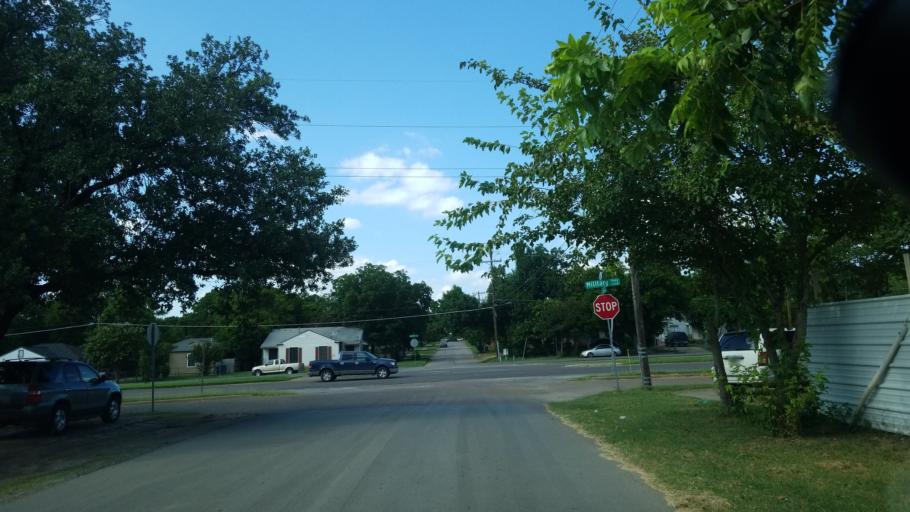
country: US
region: Texas
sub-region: Dallas County
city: Dallas
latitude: 32.7742
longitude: -96.7103
